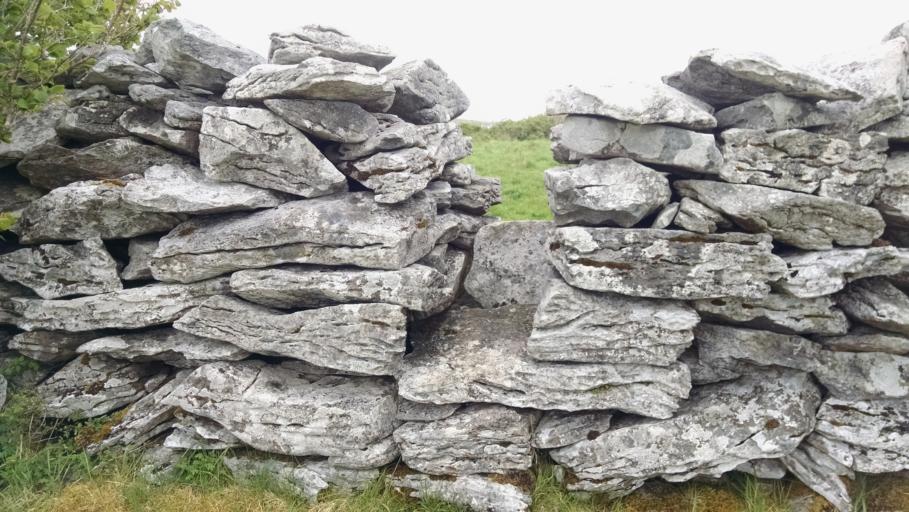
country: IE
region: Munster
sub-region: An Clar
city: Ennis
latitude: 53.0133
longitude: -9.0724
